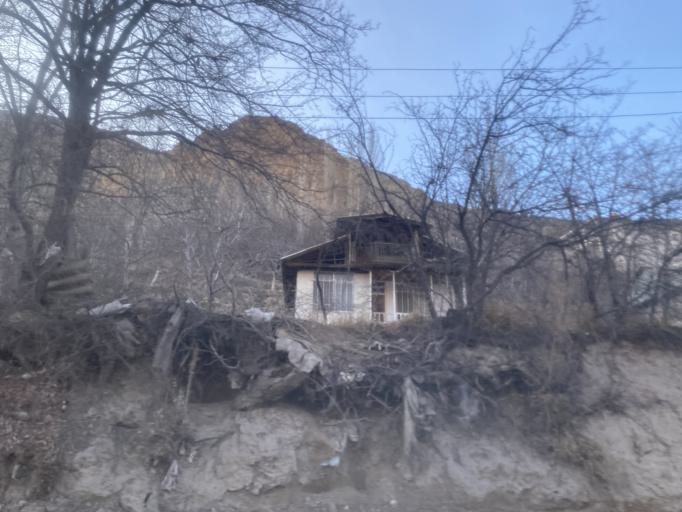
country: IR
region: Tehran
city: Damavand
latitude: 35.9024
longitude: 52.2176
